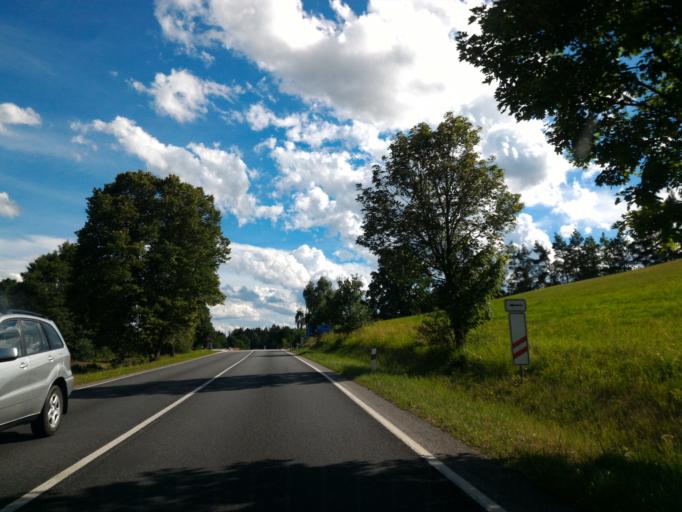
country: CZ
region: Vysocina
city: Dolni Cerekev
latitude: 49.3342
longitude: 15.4857
